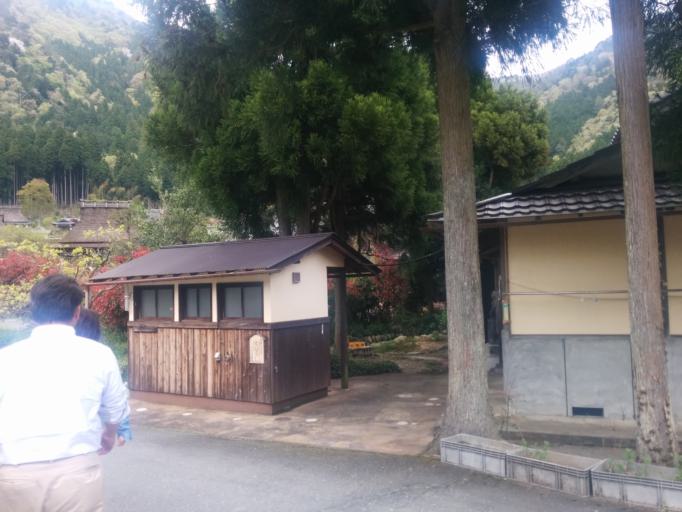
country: JP
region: Fukui
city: Obama
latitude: 35.3124
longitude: 135.6227
